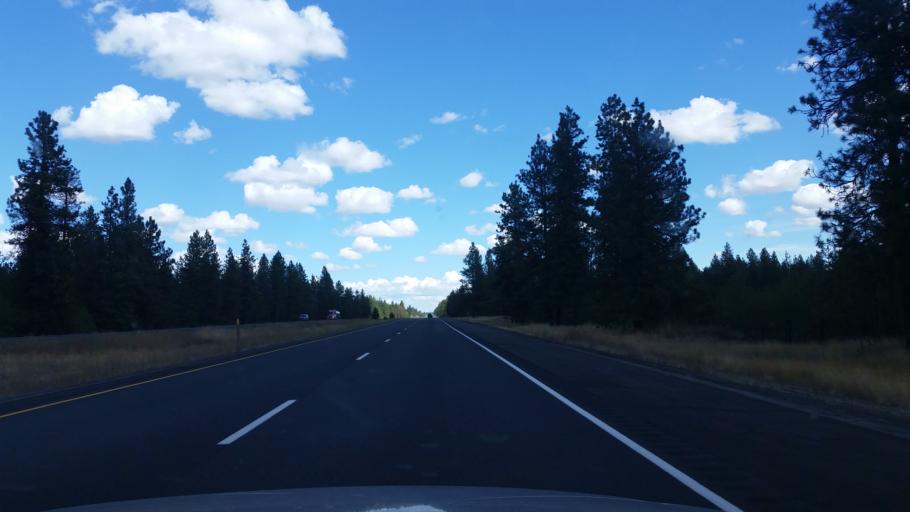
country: US
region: Washington
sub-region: Spokane County
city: Medical Lake
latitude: 47.4803
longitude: -117.7258
